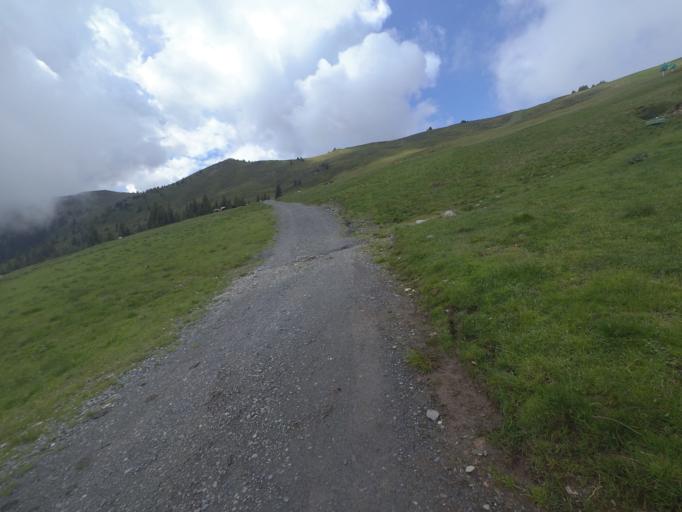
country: AT
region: Salzburg
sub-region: Politischer Bezirk Zell am See
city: Viehhofen
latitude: 47.4016
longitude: 12.7077
